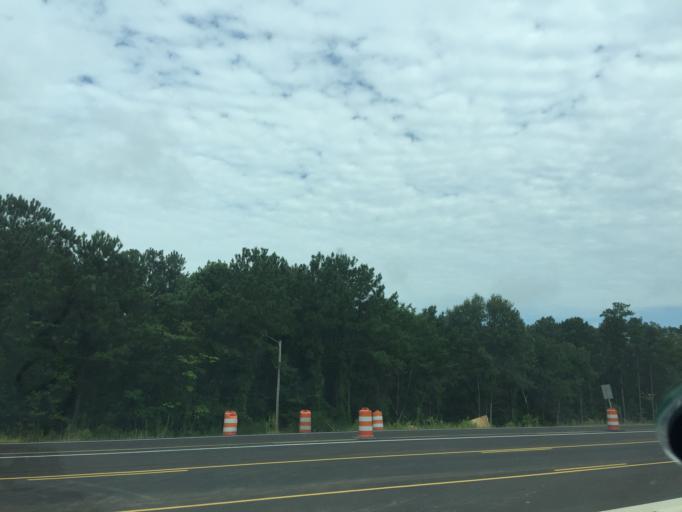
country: US
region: Mississippi
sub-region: Rankin County
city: Brandon
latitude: 32.2753
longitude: -89.9938
